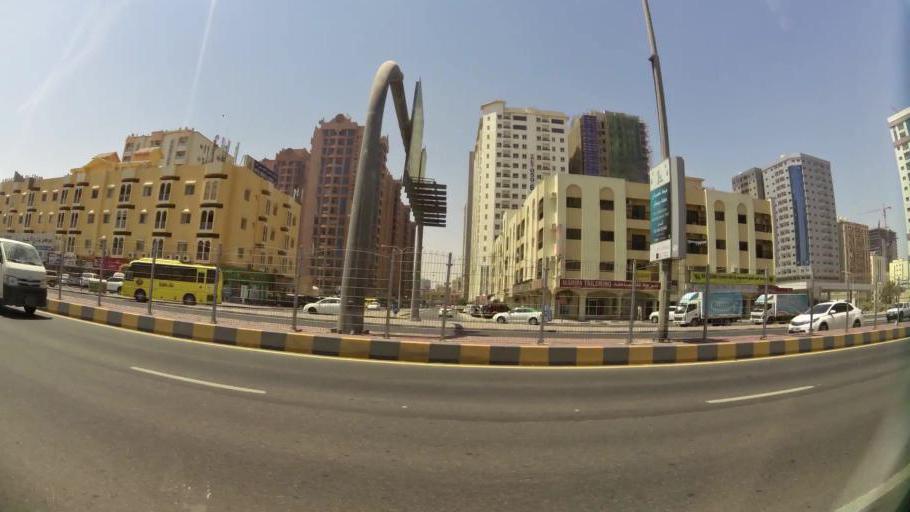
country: AE
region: Ajman
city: Ajman
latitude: 25.3894
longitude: 55.4591
